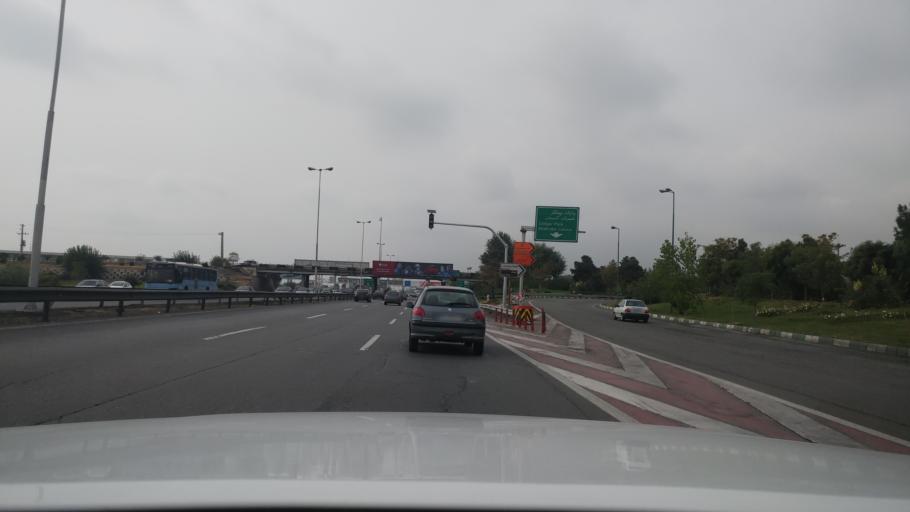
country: IR
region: Tehran
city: Shahr-e Qods
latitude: 35.7158
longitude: 51.2428
